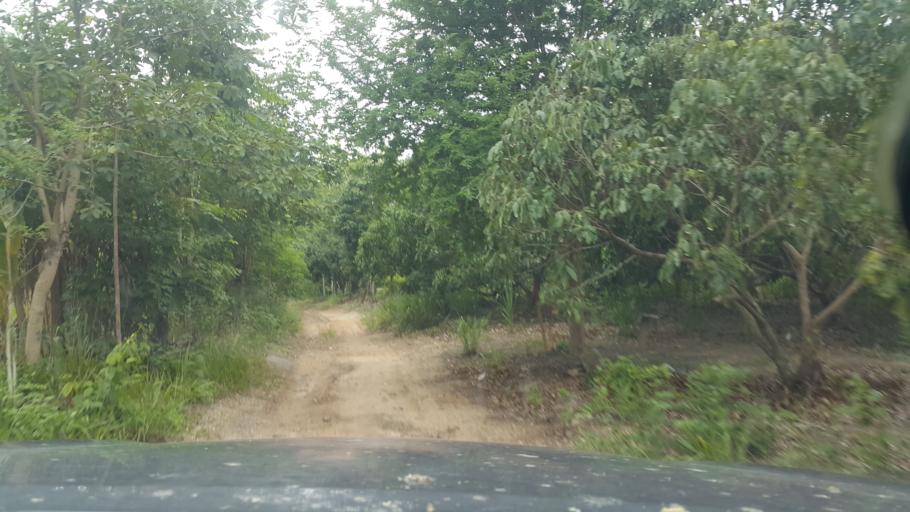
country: TH
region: Chiang Mai
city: San Pa Tong
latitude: 18.6815
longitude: 98.8417
